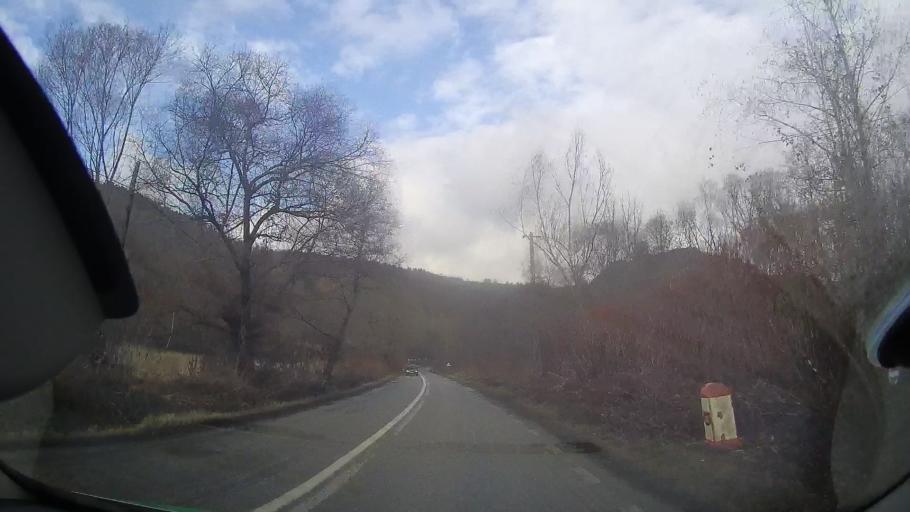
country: RO
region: Alba
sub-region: Comuna Ocolis
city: Ocolis
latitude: 46.4363
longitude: 23.4535
